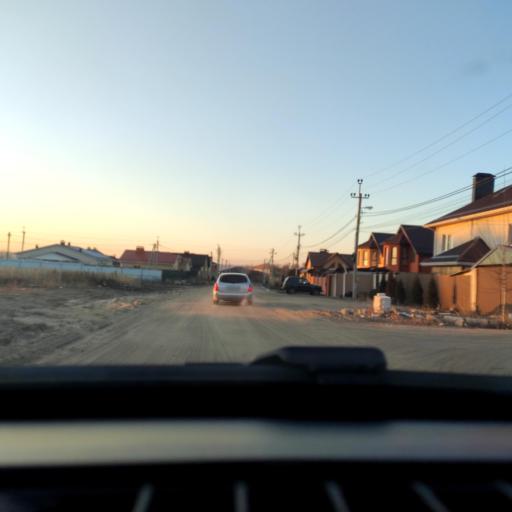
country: RU
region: Voronezj
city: Podgornoye
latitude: 51.7251
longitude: 39.1342
